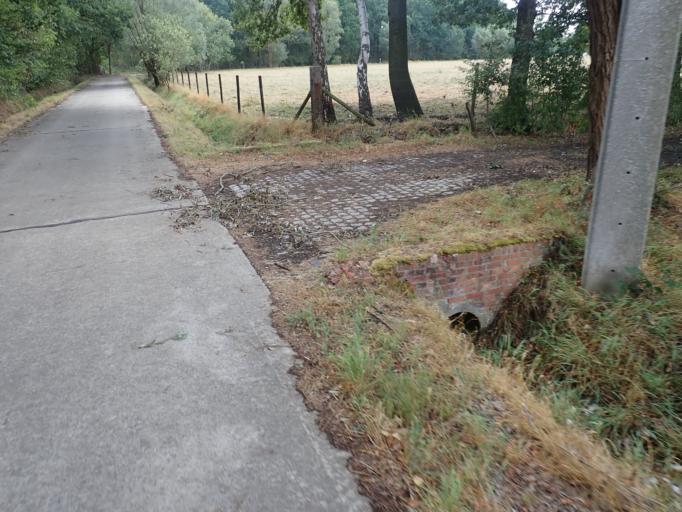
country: BE
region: Flanders
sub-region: Provincie Antwerpen
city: Heist-op-den-Berg
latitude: 51.1047
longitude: 4.7029
